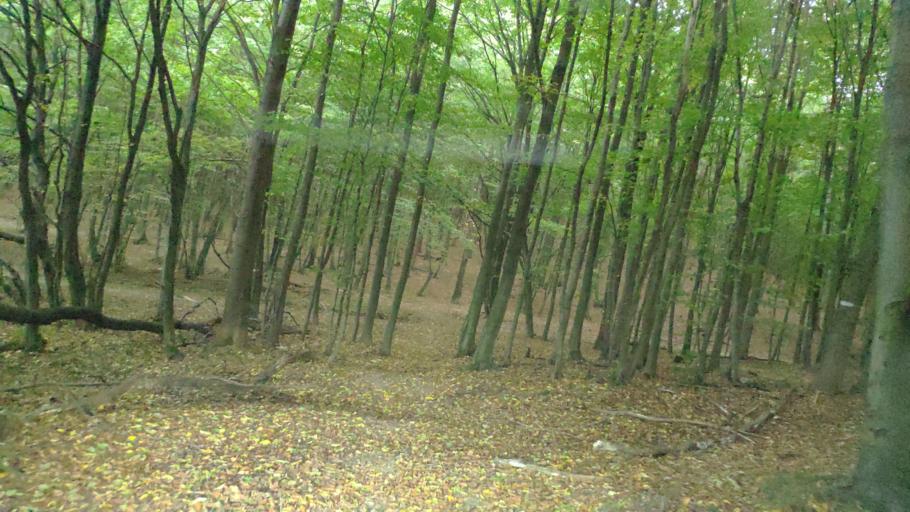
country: SK
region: Kosicky
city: Kosice
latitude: 48.7009
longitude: 21.2001
